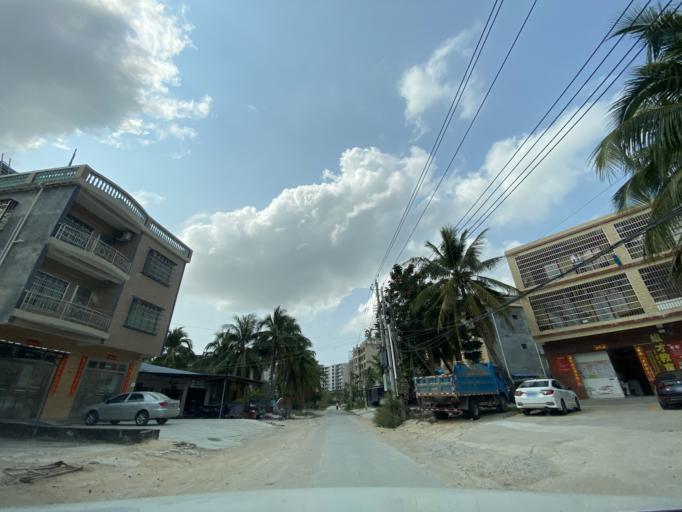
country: CN
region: Hainan
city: Yingzhou
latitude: 18.4188
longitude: 109.8493
